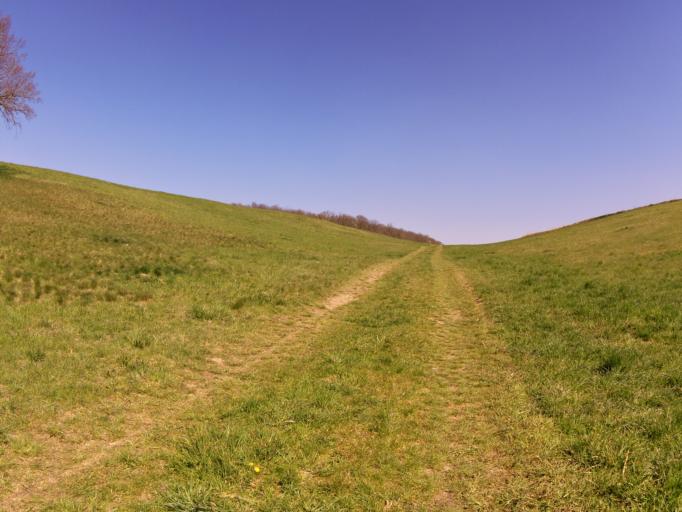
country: DE
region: Bavaria
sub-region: Regierungsbezirk Unterfranken
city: Rottendorf
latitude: 49.8237
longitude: 10.0518
